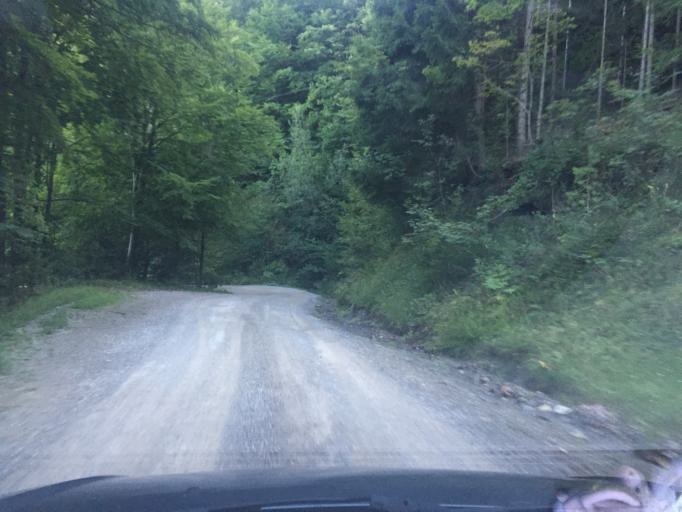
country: SI
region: Ravne na Koroskem
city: Kotlje
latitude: 46.4612
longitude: 14.9952
